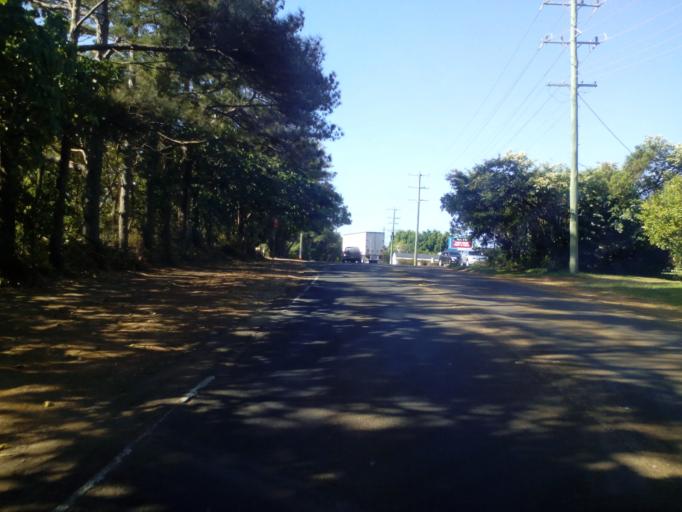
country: AU
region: New South Wales
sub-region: Tweed
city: Kingscliff
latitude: -28.2663
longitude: 153.5658
